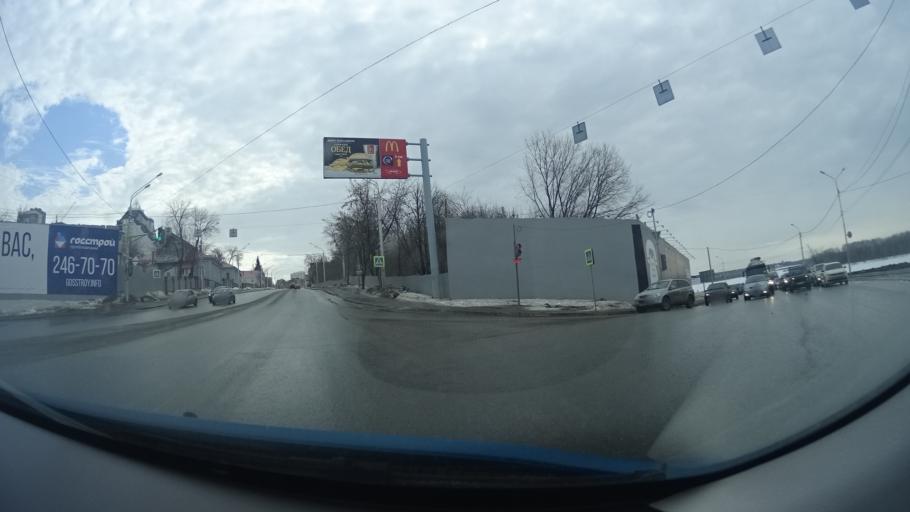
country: RU
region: Bashkortostan
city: Ufa
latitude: 54.7099
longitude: 55.9645
